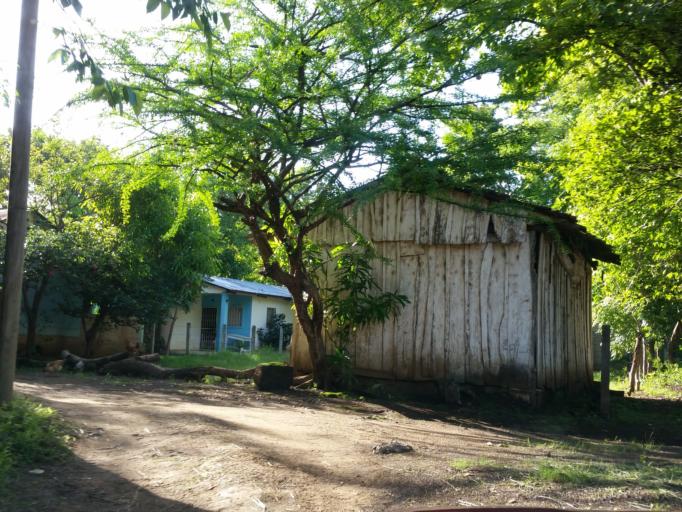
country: NI
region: Managua
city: Managua
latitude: 12.0787
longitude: -86.2263
